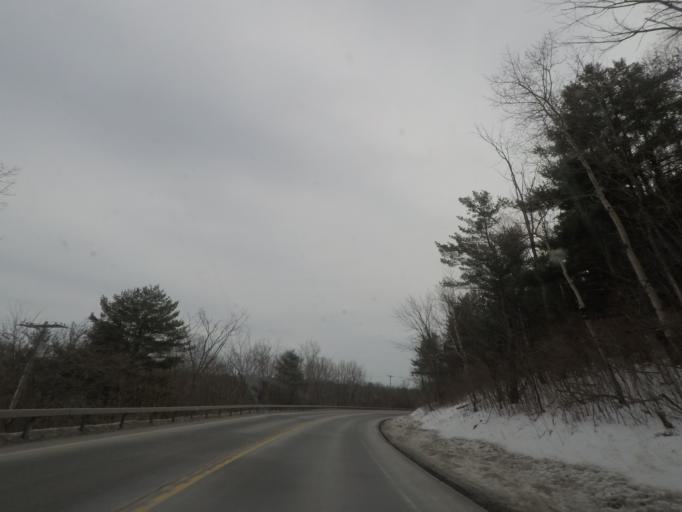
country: US
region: New York
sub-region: Albany County
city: Voorheesville
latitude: 42.5967
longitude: -73.9892
